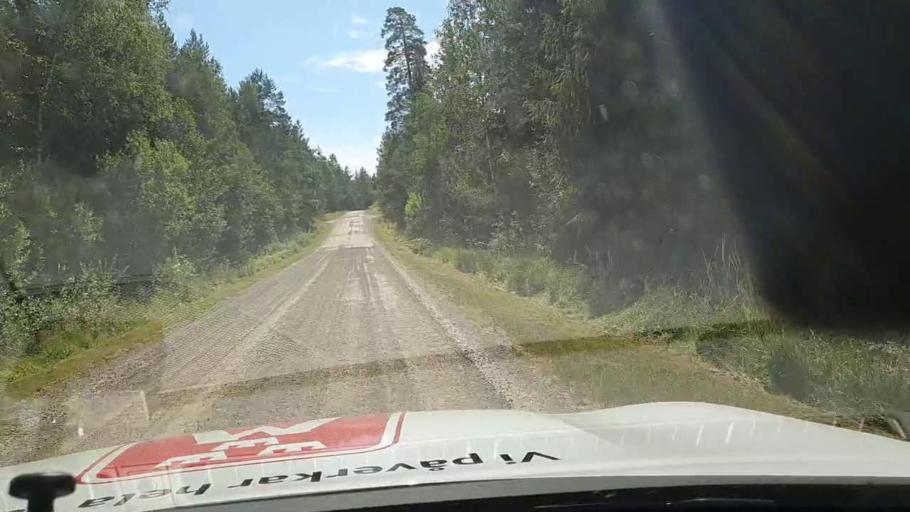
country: SE
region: Soedermanland
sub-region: Strangnas Kommun
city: Akers Styckebruk
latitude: 59.2184
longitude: 16.9085
